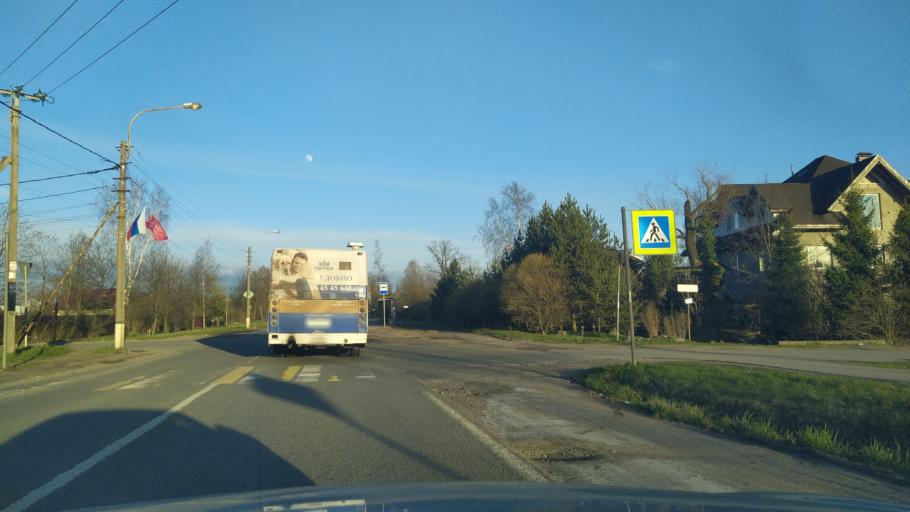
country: RU
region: St.-Petersburg
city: Aleksandrovskaya
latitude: 59.7362
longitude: 30.3330
